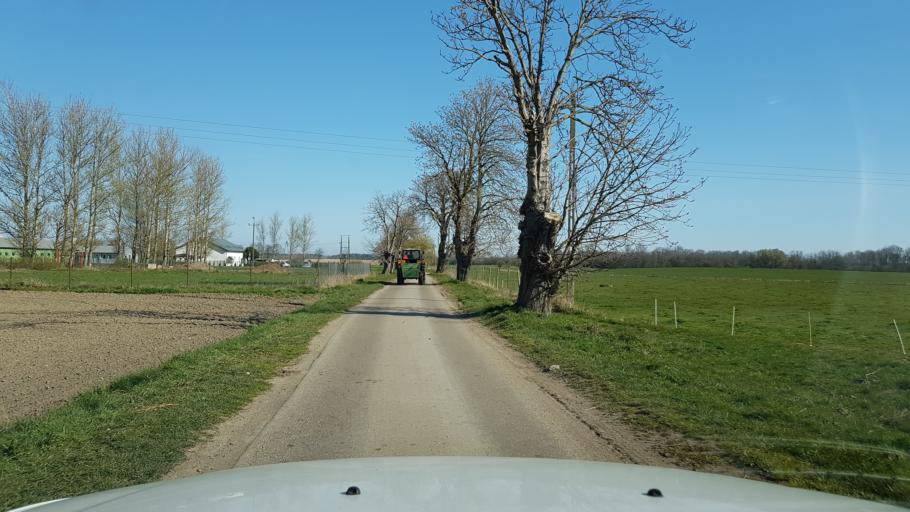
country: PL
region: West Pomeranian Voivodeship
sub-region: Powiat kolobrzeski
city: Ustronie Morskie
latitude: 54.2149
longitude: 15.8477
